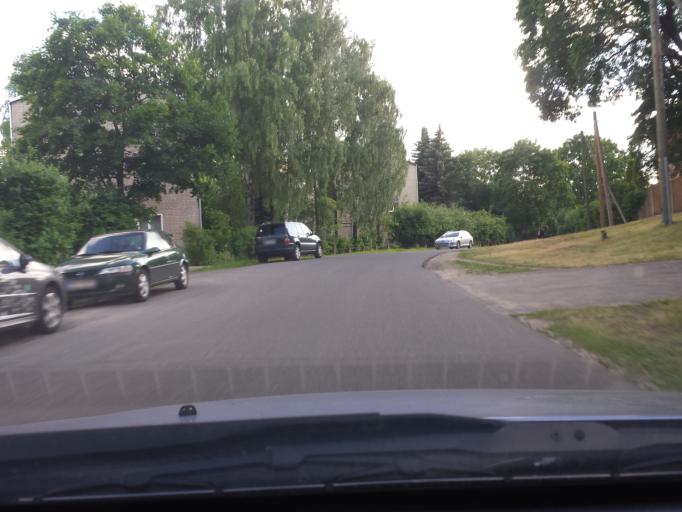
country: LV
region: Riga
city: Riga
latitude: 56.9594
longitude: 24.0631
